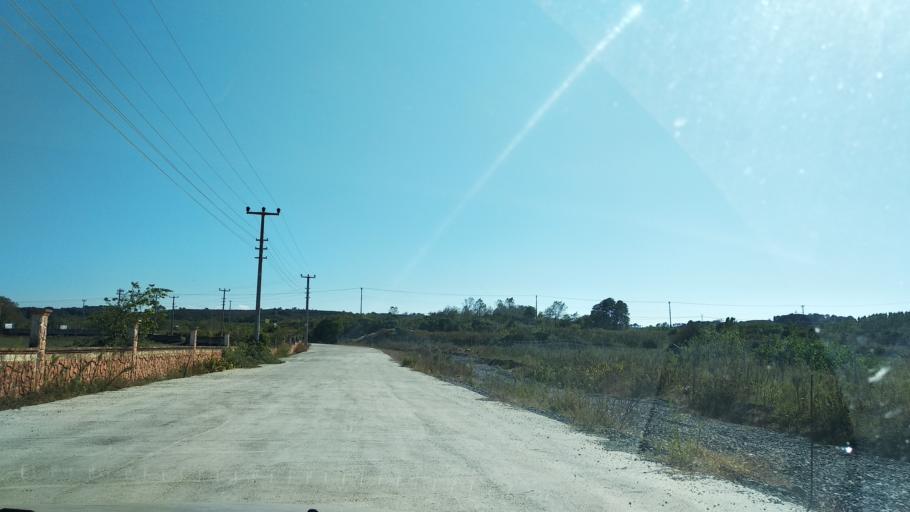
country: TR
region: Sakarya
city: Karasu
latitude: 41.1208
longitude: 30.6078
